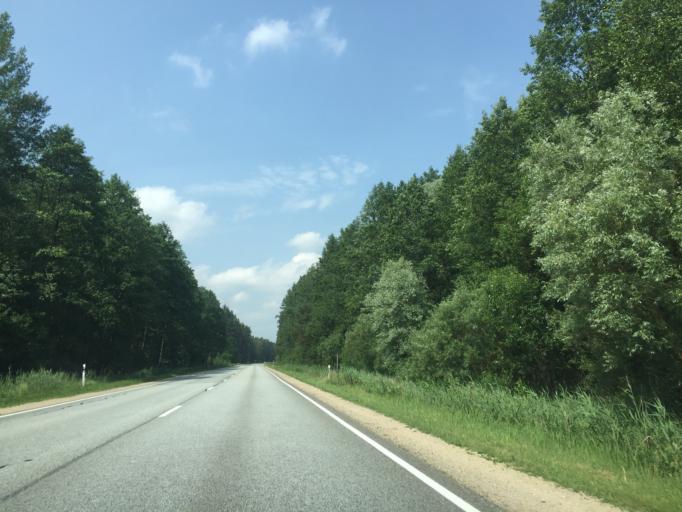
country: LV
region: Kekava
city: Balozi
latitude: 56.8254
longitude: 24.0654
